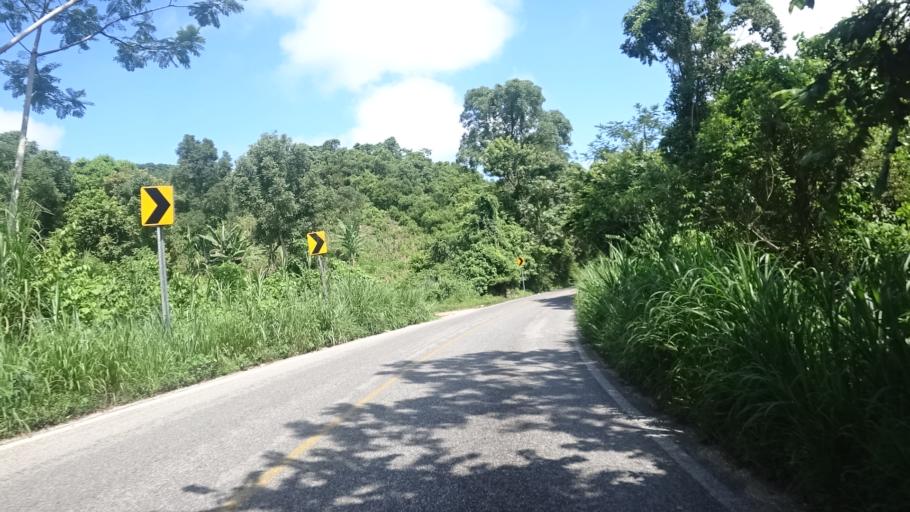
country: MX
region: Chiapas
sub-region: Palenque
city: Doctor Samuel Leon Brindis
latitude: 17.4570
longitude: -91.9656
